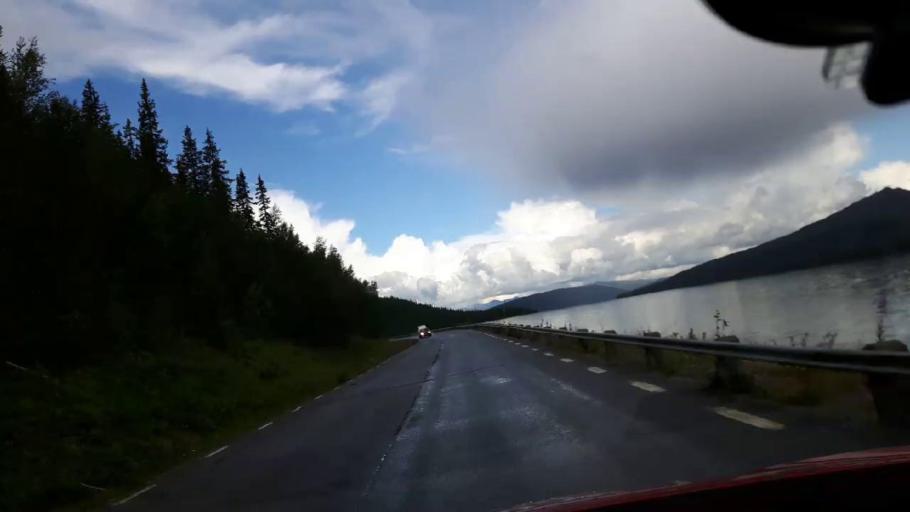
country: SE
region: Vaesterbotten
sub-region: Vilhelmina Kommun
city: Sjoberg
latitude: 64.9799
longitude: 15.3103
